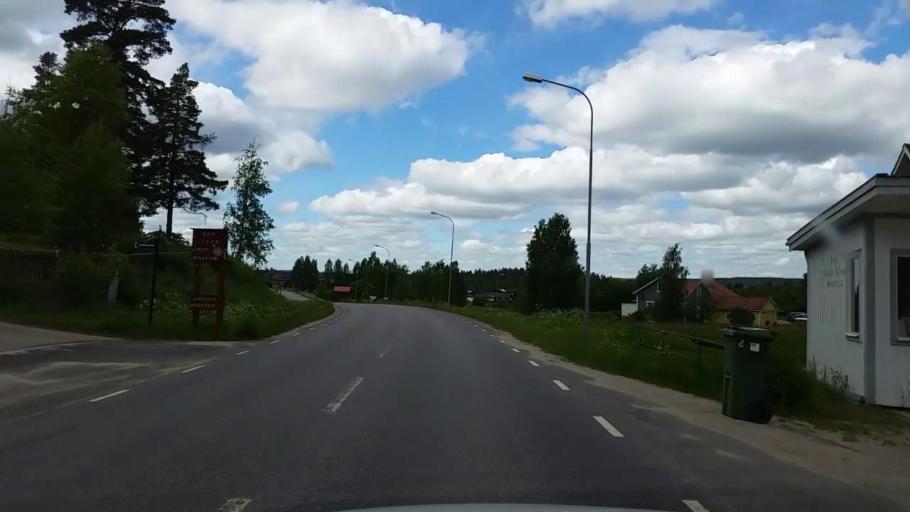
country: SE
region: Gaevleborg
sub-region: Ovanakers Kommun
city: Alfta
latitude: 61.3922
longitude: 16.0447
